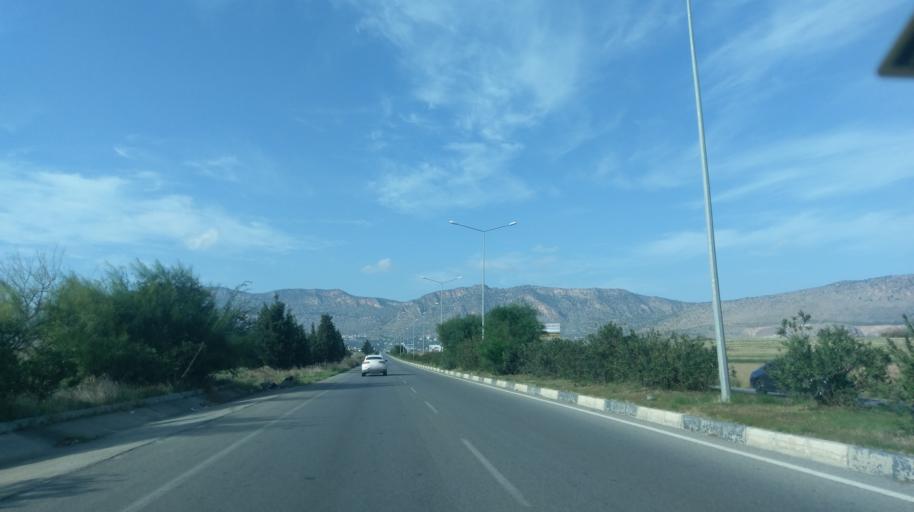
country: CY
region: Keryneia
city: Kyrenia
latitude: 35.2629
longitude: 33.2952
